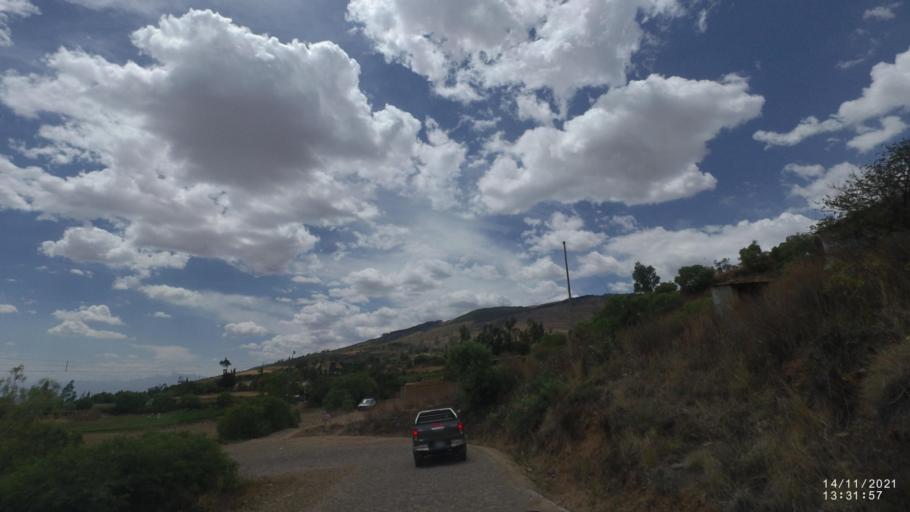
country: BO
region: Cochabamba
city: Colomi
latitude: -17.3958
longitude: -65.9830
